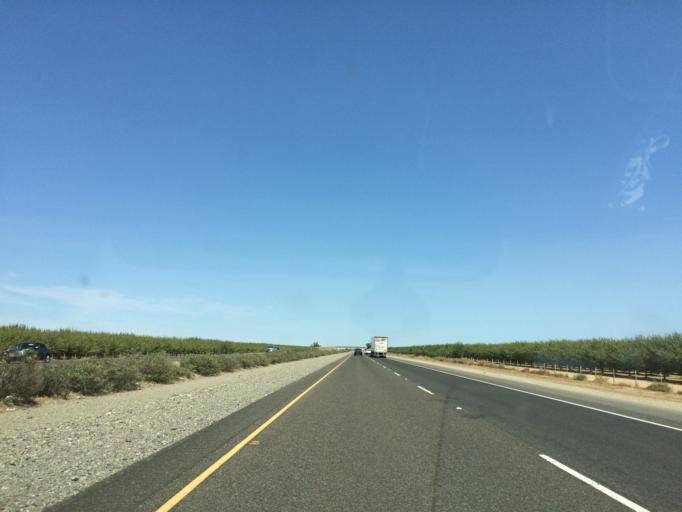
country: US
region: California
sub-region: Glenn County
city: Orland
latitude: 39.6719
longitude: -122.2045
